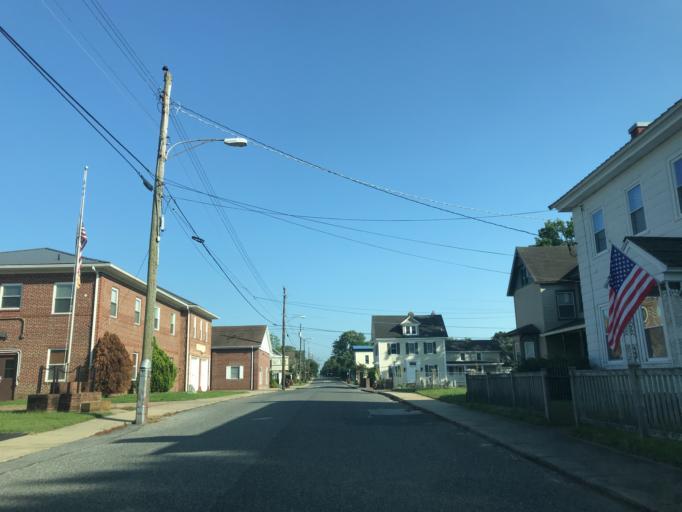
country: US
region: Maryland
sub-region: Wicomico County
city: Hebron
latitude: 38.5414
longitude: -75.7200
